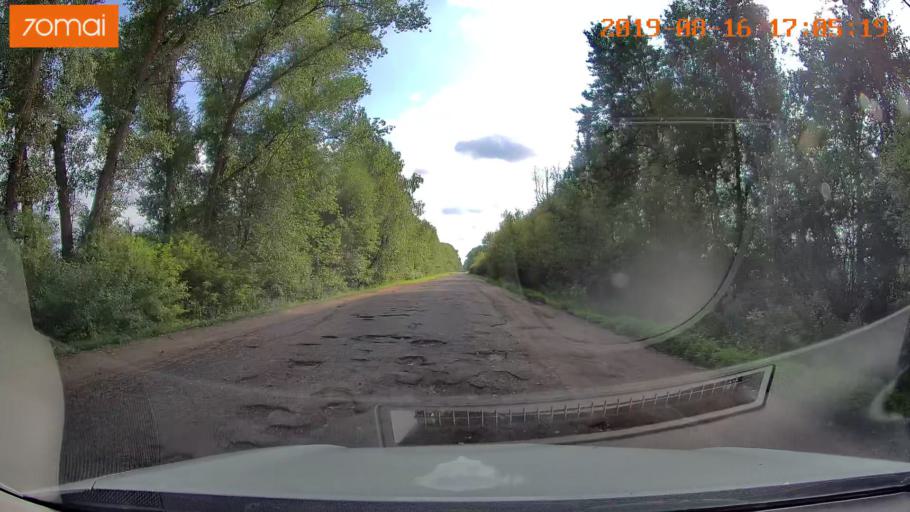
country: BY
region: Mogilev
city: Yalizava
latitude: 53.2381
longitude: 28.9448
